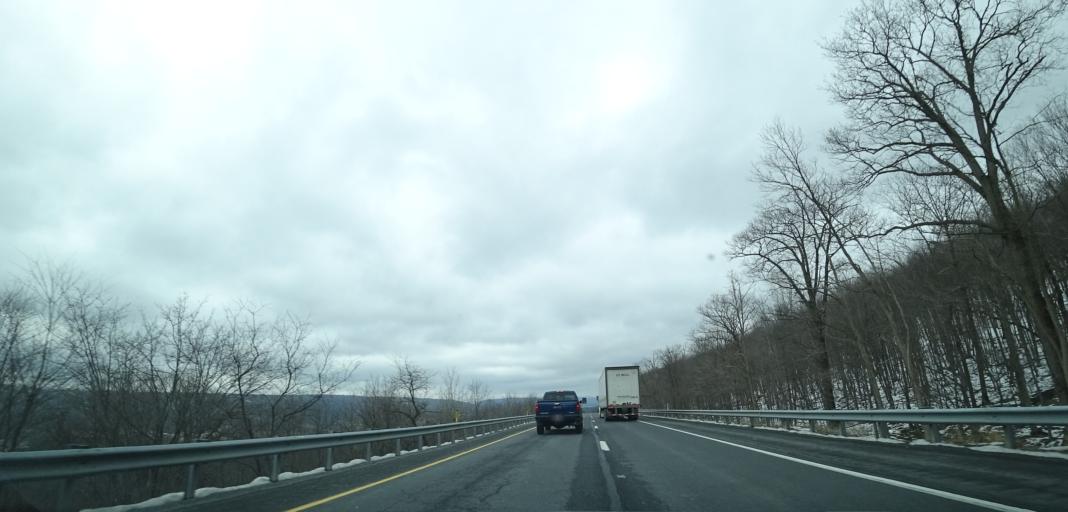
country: US
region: Pennsylvania
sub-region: Bedford County
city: Earlston
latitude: 39.8900
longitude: -78.2435
